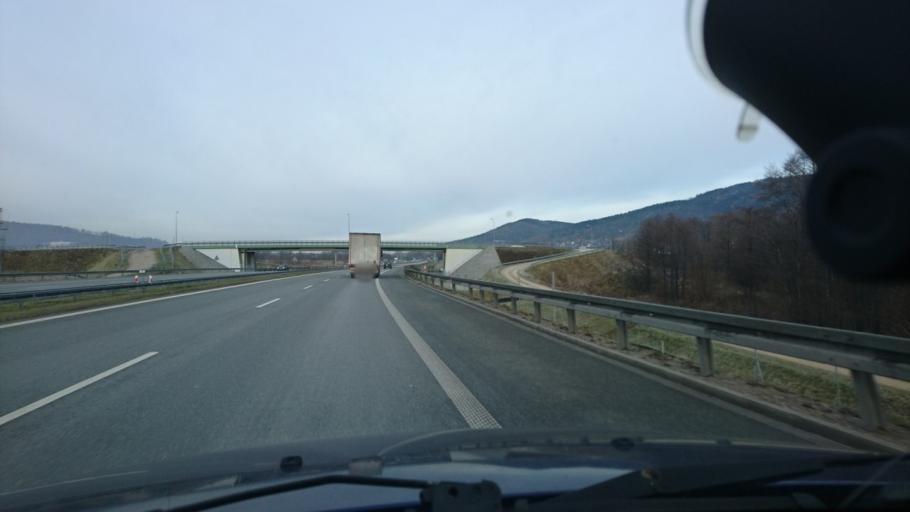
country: PL
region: Silesian Voivodeship
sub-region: Powiat bielski
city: Wilkowice
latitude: 49.7478
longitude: 19.0887
